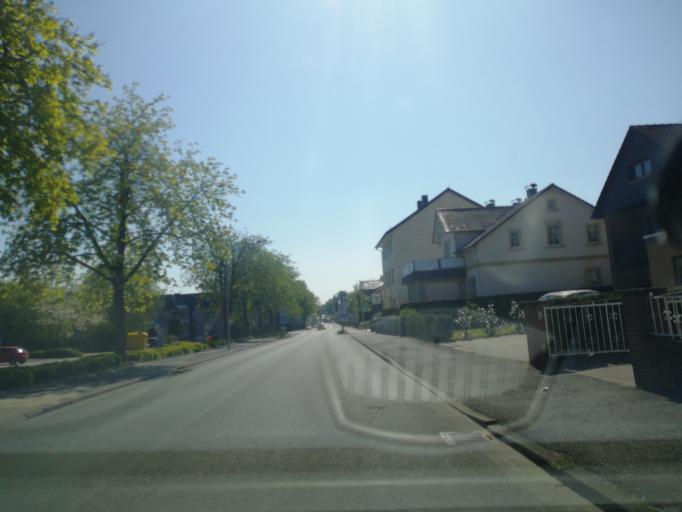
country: DE
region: Lower Saxony
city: Bad Rothenfelde
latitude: 52.1150
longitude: 8.1630
